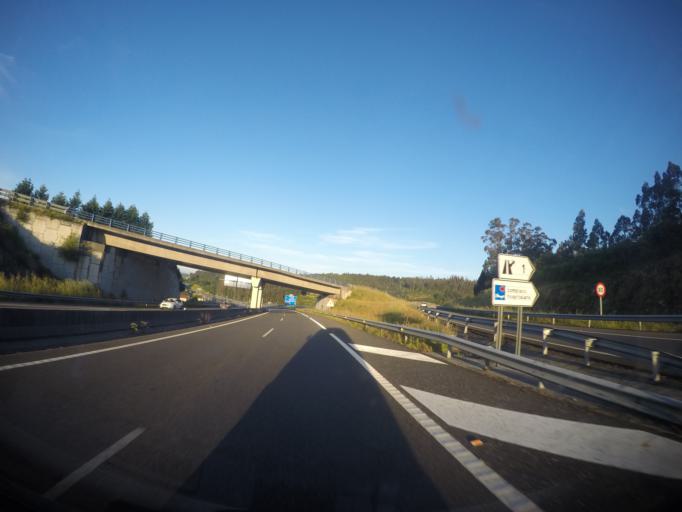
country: ES
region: Galicia
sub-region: Provincia da Coruna
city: Oroso
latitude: 42.9643
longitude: -8.4544
